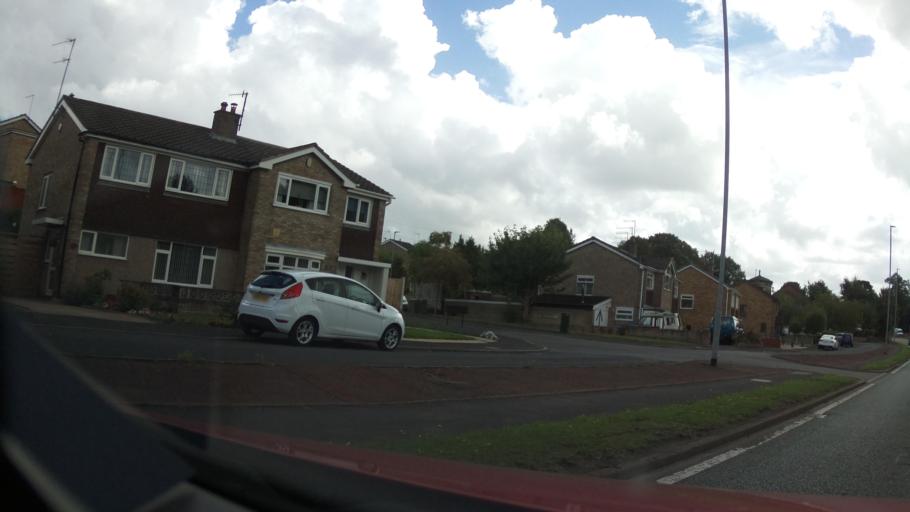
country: GB
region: England
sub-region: Stoke-on-Trent
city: Stoke-on-Trent
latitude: 52.9685
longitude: -2.2002
